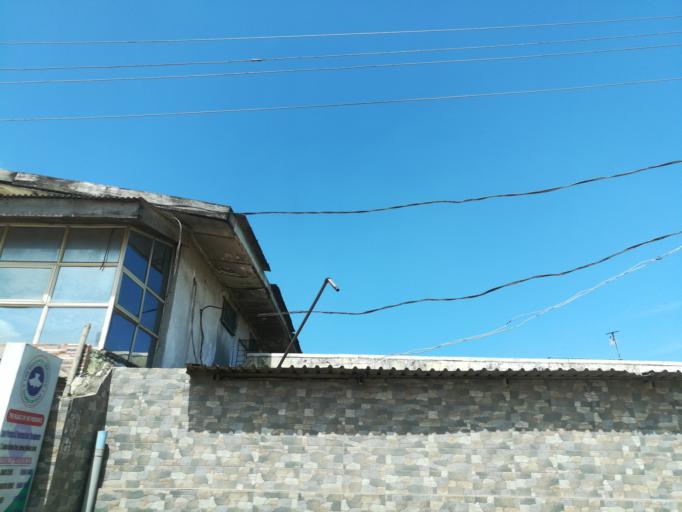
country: NG
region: Lagos
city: Oshodi
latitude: 6.5664
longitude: 3.3322
